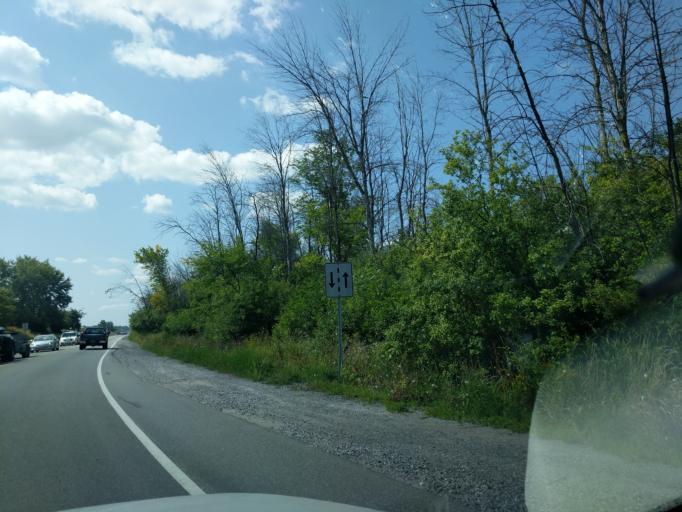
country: CA
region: Quebec
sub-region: Outaouais
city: Gatineau
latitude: 45.4445
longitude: -75.7800
